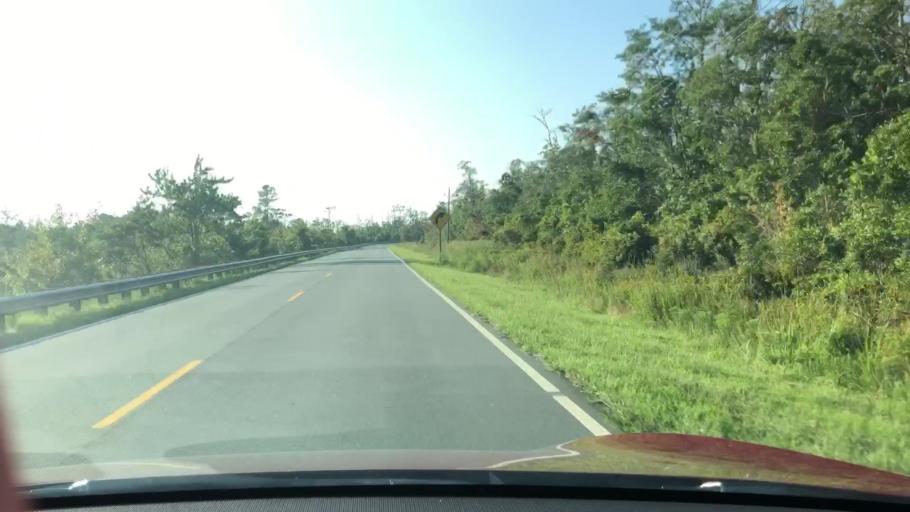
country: US
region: North Carolina
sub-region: Dare County
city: Manteo
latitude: 35.8293
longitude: -75.8080
